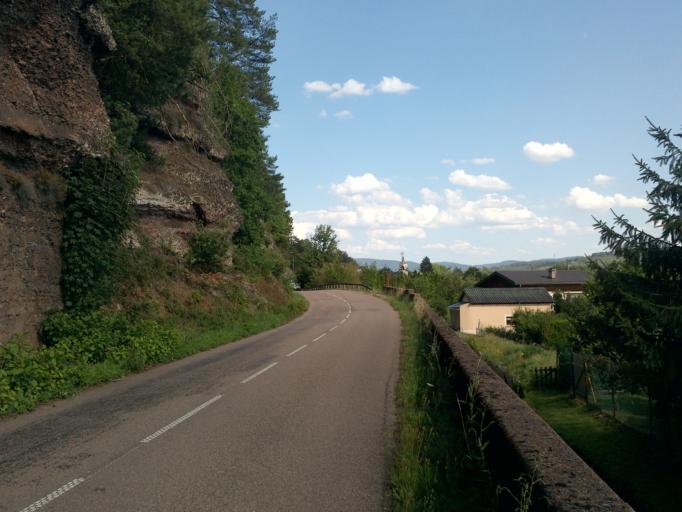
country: FR
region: Lorraine
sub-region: Departement des Vosges
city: Arches
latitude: 48.1266
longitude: 6.5241
